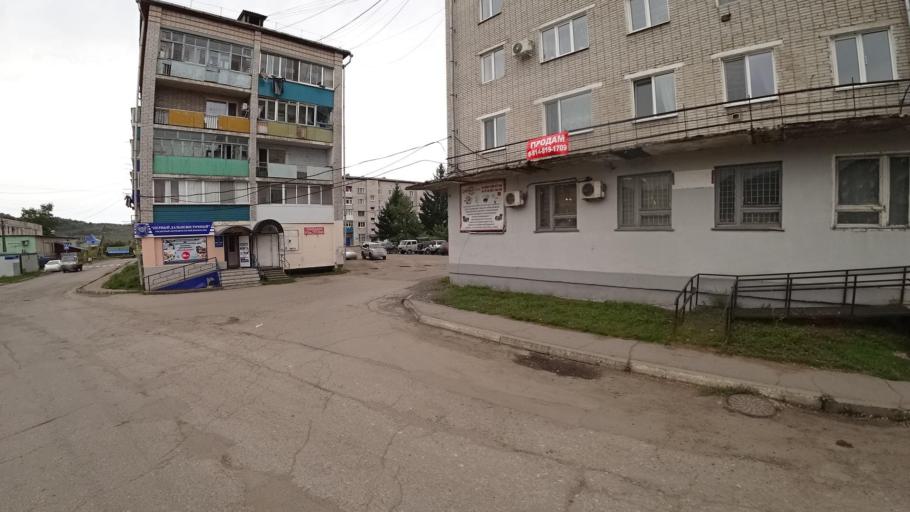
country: RU
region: Jewish Autonomous Oblast
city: Khingansk
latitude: 49.0097
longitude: 131.0525
